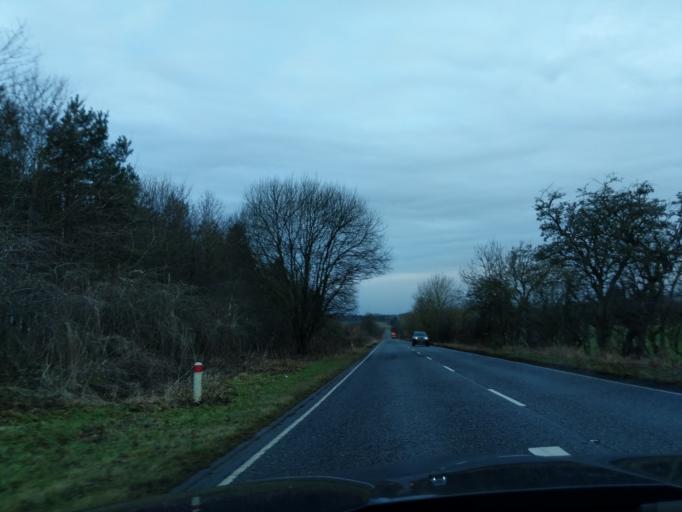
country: GB
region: England
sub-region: Northumberland
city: Rothley
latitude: 55.1381
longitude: -1.9711
